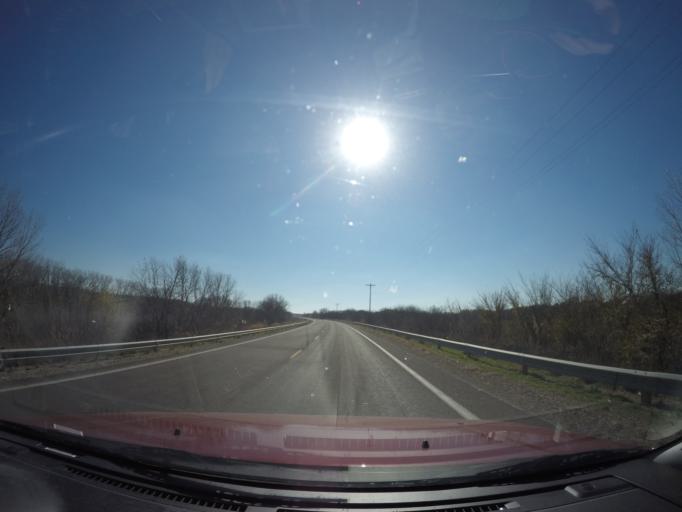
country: US
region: Kansas
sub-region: Morris County
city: Council Grove
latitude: 38.7360
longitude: -96.5012
